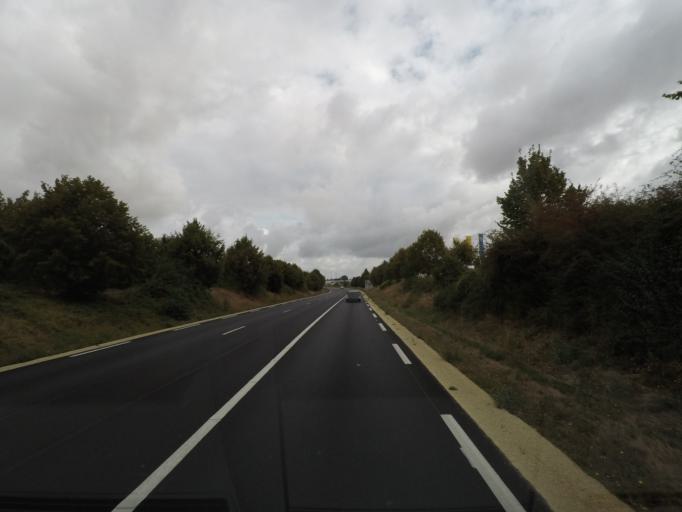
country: FR
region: Poitou-Charentes
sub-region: Departement des Deux-Sevres
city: Celles-sur-Belle
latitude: 46.2655
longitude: -0.2270
